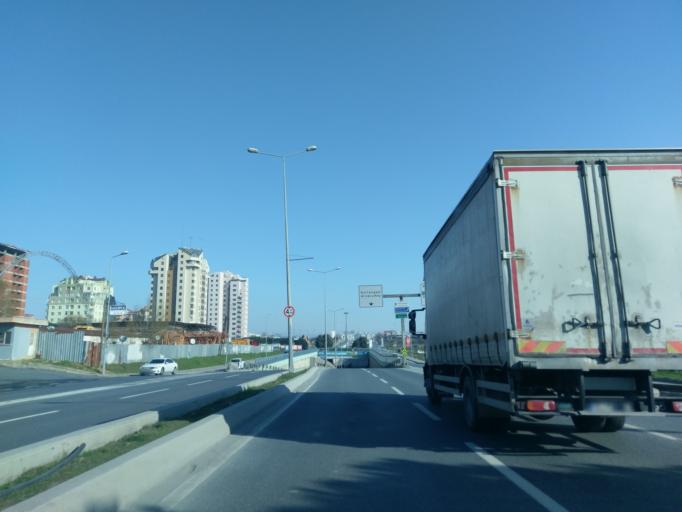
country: TR
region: Istanbul
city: Basaksehir
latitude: 41.1057
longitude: 28.7944
